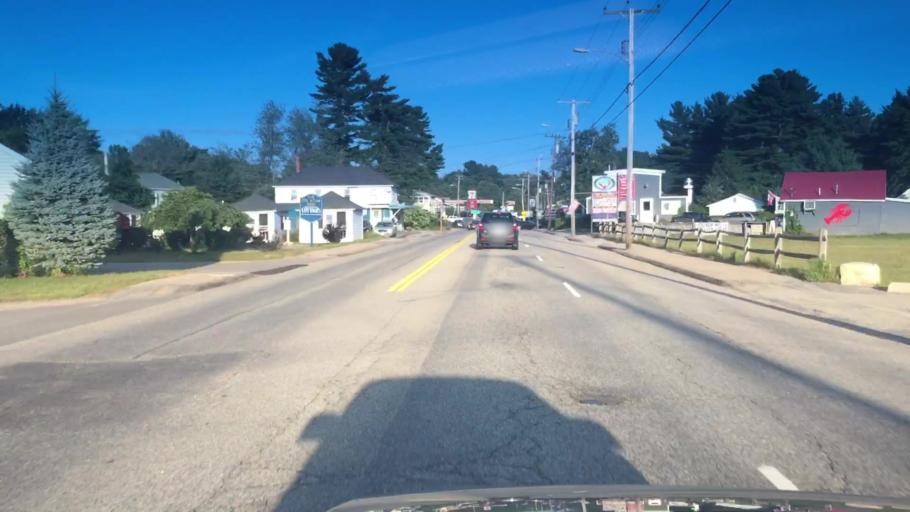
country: US
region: Maine
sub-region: York County
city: Saco
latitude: 43.5078
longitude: -70.4117
